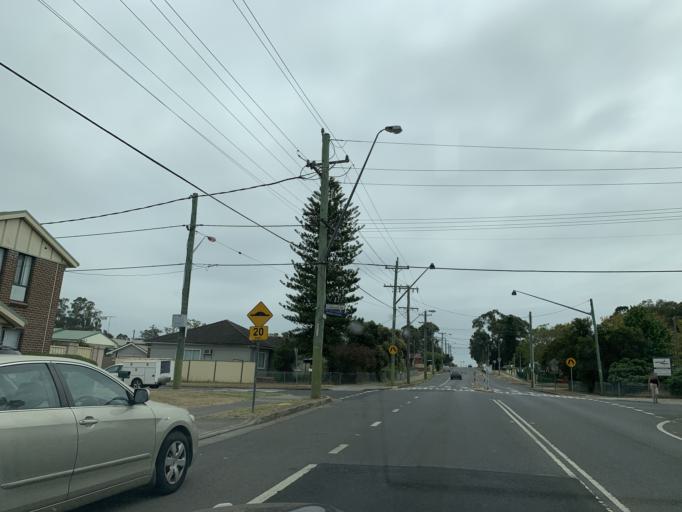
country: AU
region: New South Wales
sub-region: Blacktown
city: Doonside
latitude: -33.7589
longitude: 150.8703
